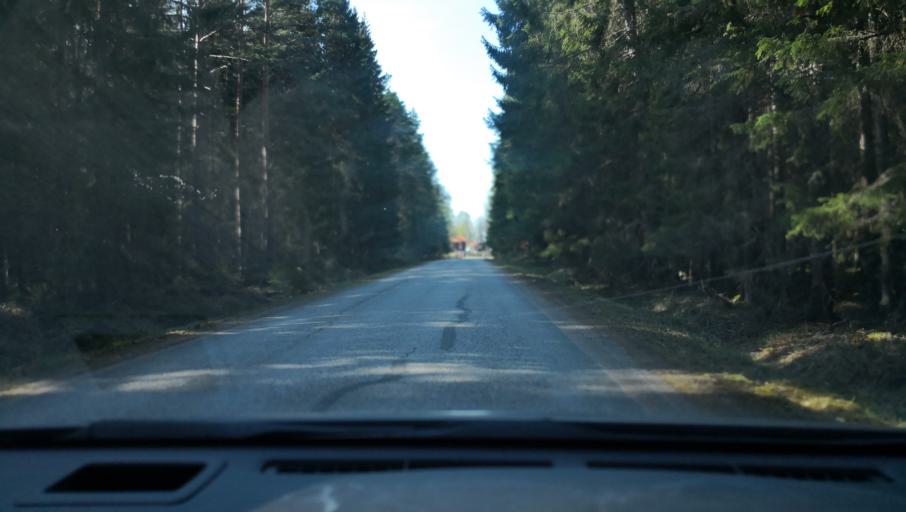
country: SE
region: Uppsala
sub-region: Heby Kommun
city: Tarnsjo
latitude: 60.2812
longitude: 16.8866
